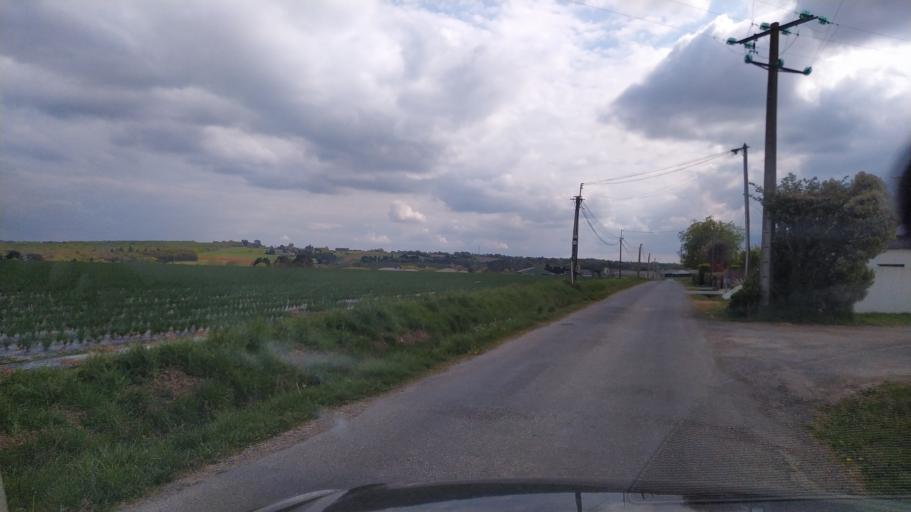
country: FR
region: Brittany
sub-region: Departement du Finistere
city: Bodilis
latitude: 48.5076
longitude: -4.1018
